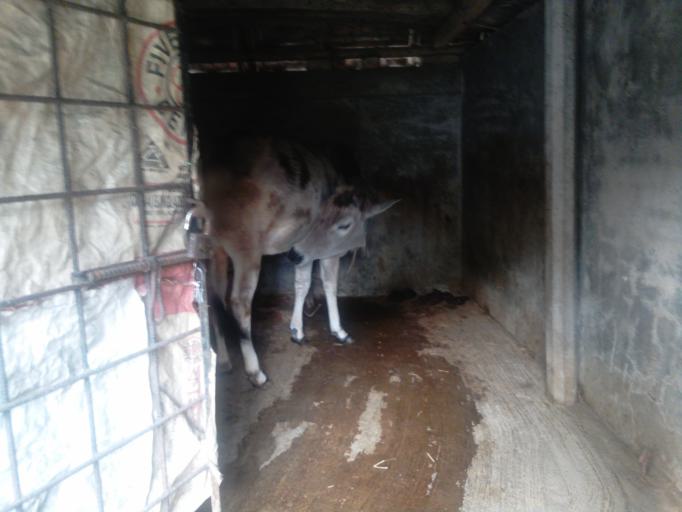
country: BD
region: Khulna
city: Kesabpur
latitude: 22.7719
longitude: 89.2529
